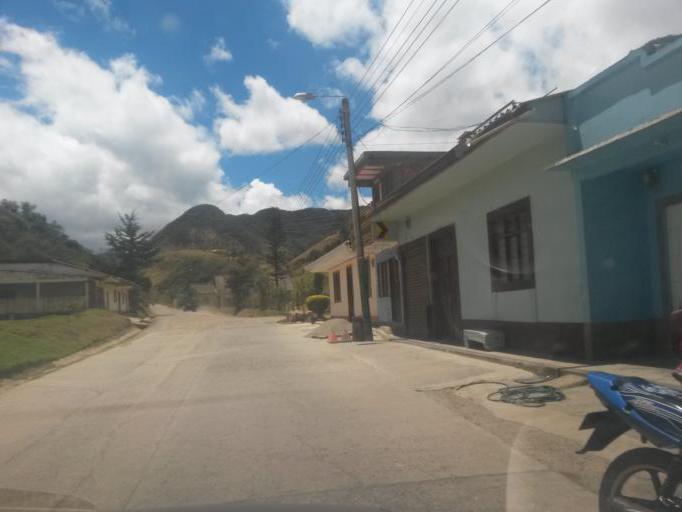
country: CO
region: Cauca
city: Silvia
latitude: 2.6159
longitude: -76.3703
